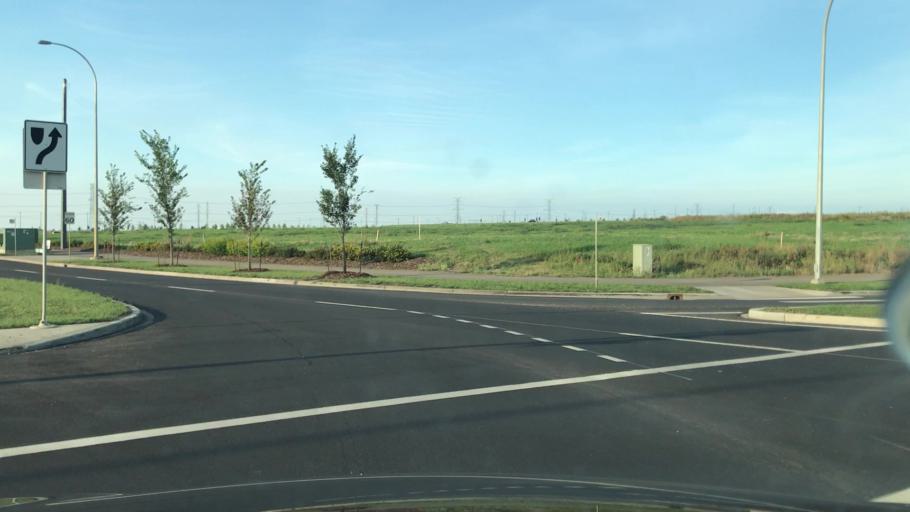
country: CA
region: Alberta
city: Beaumont
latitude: 53.4248
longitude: -113.4179
